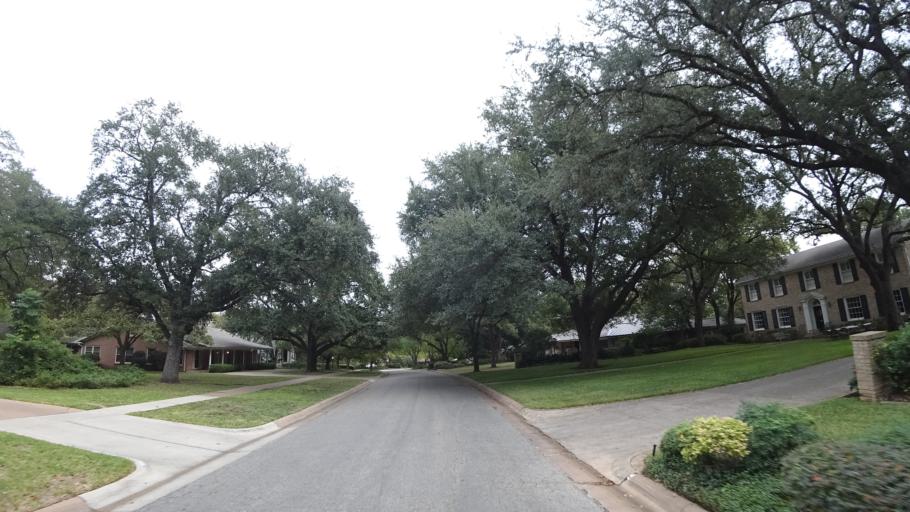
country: US
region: Texas
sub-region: Travis County
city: Austin
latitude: 30.2918
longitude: -97.7543
